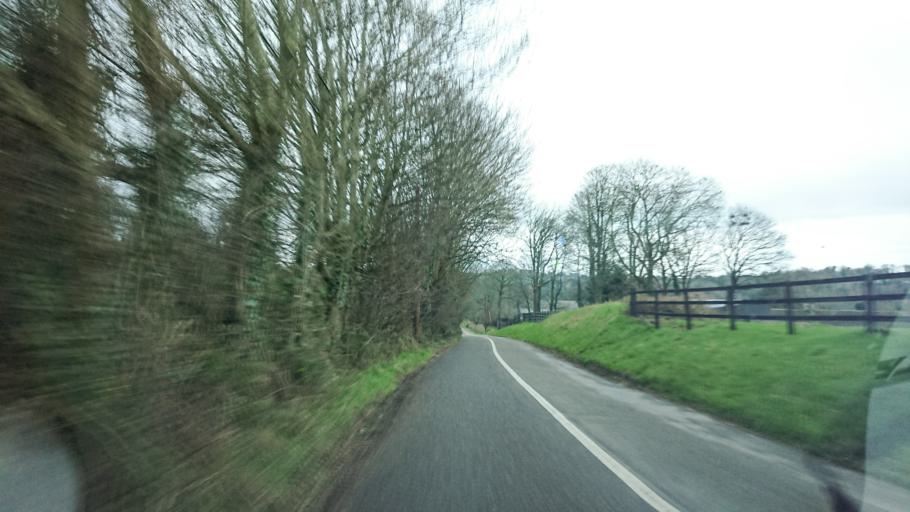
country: IE
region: Munster
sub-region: Waterford
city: Portlaw
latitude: 52.1780
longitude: -7.4062
